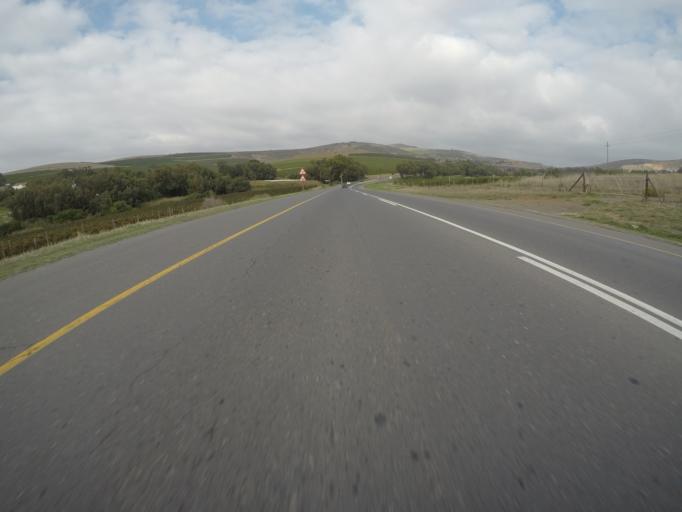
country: ZA
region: Western Cape
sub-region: City of Cape Town
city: Sunset Beach
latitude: -33.8204
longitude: 18.5714
